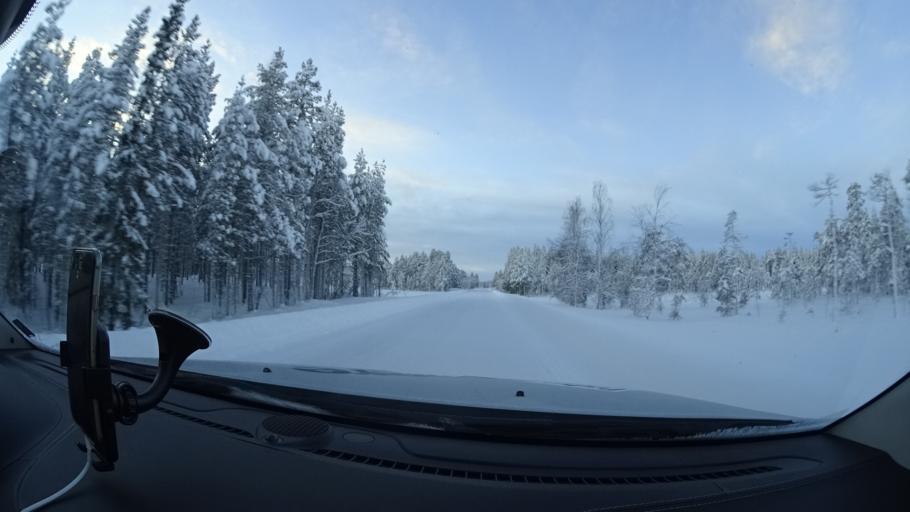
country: SE
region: Norrbotten
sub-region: Jokkmokks Kommun
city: Jokkmokk
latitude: 66.0265
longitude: 19.8976
